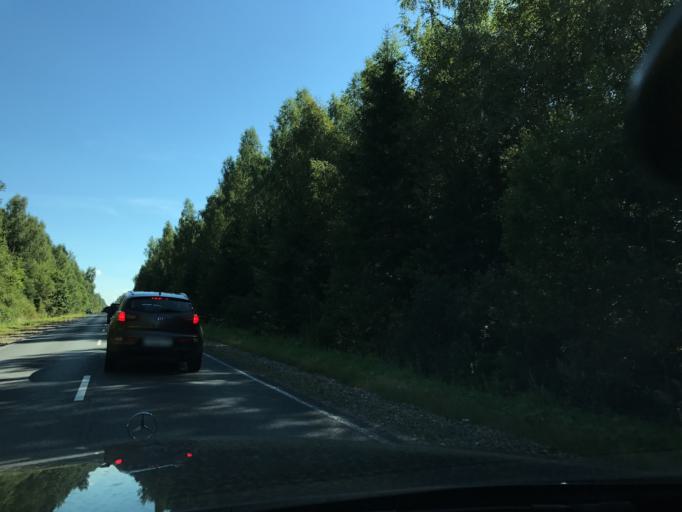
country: RU
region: Vladimir
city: Kol'chugino
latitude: 56.2810
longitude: 39.2777
